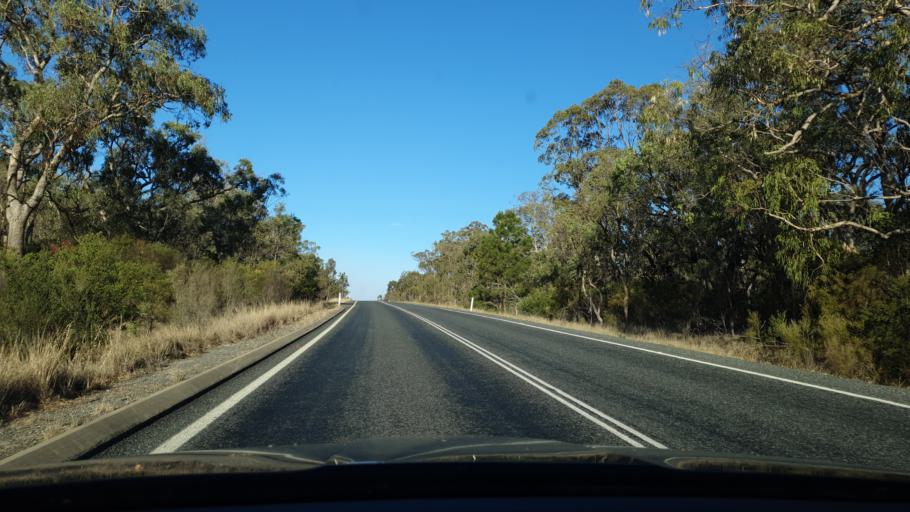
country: AU
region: Queensland
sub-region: Southern Downs
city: Stanthorpe
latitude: -28.6425
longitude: 151.9359
